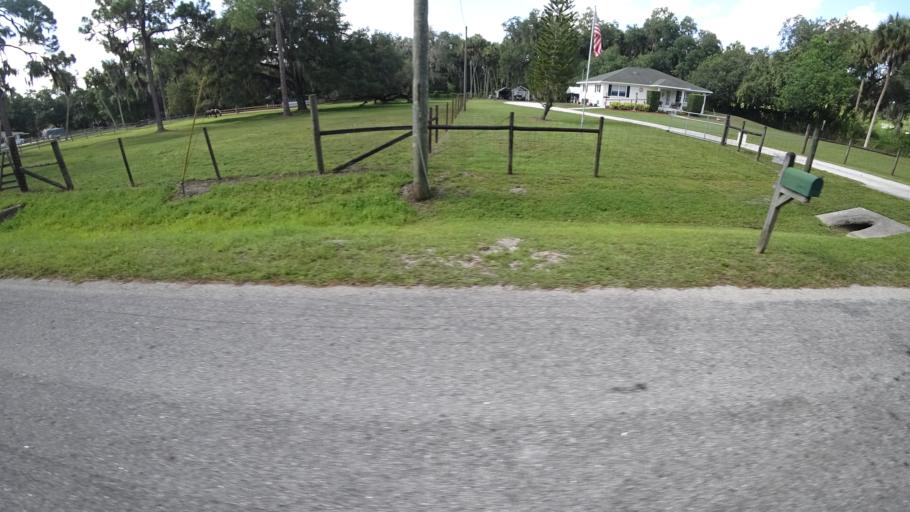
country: US
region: Florida
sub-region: Manatee County
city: Ellenton
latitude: 27.4830
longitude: -82.4770
